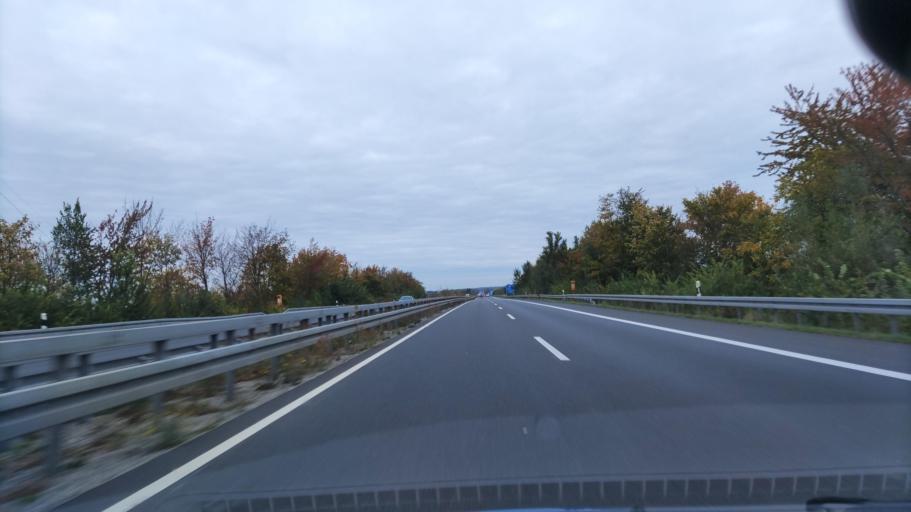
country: DE
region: Lower Saxony
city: Leiferde
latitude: 52.1667
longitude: 10.4966
